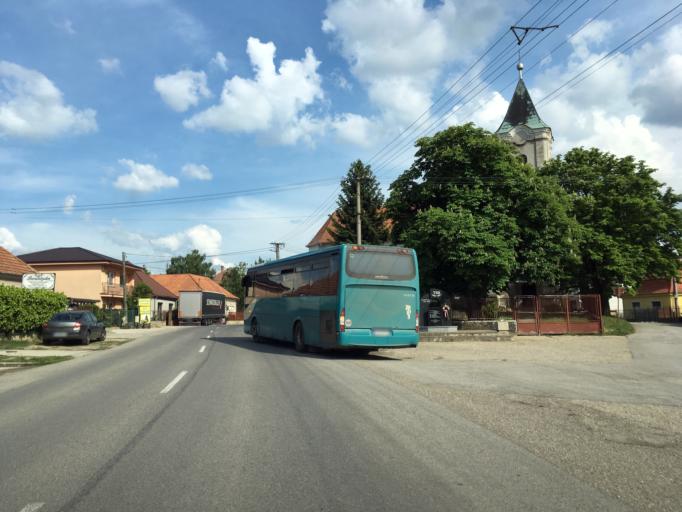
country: HU
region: Komarom-Esztergom
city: Almasfuzito
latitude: 47.7873
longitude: 18.2722
